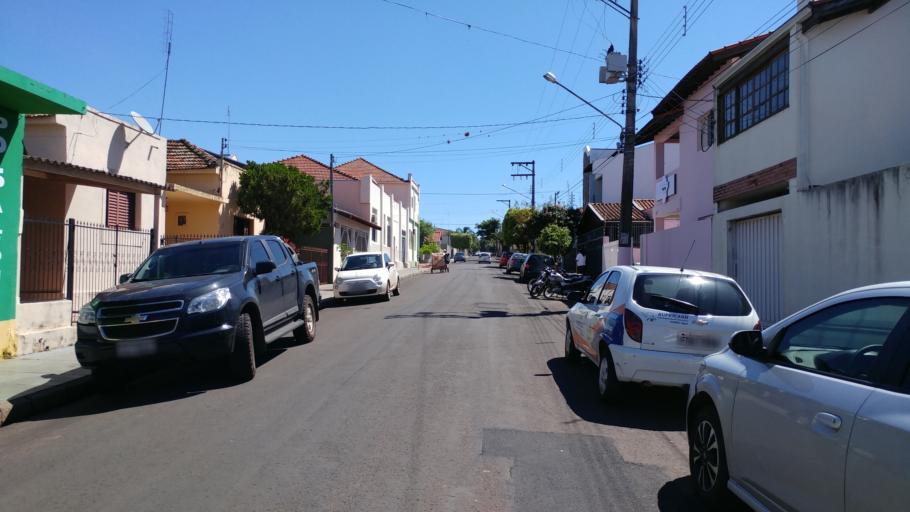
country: BR
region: Sao Paulo
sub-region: Paraguacu Paulista
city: Paraguacu Paulista
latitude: -22.4175
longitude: -50.5754
